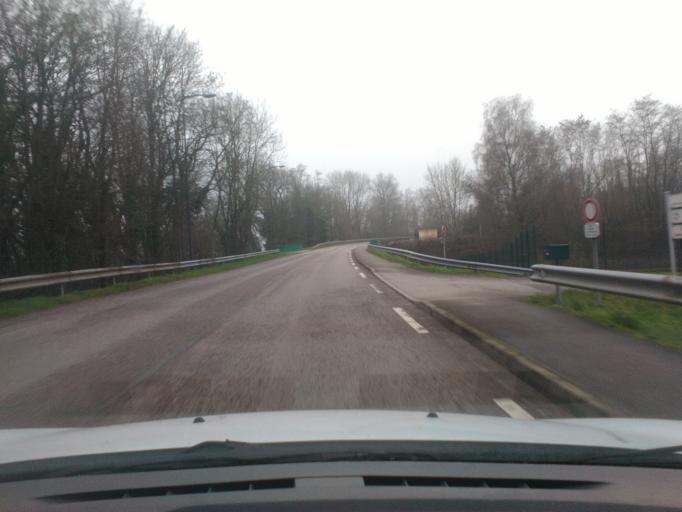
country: FR
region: Lorraine
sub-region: Departement des Vosges
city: Golbey
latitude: 48.2091
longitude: 6.4413
